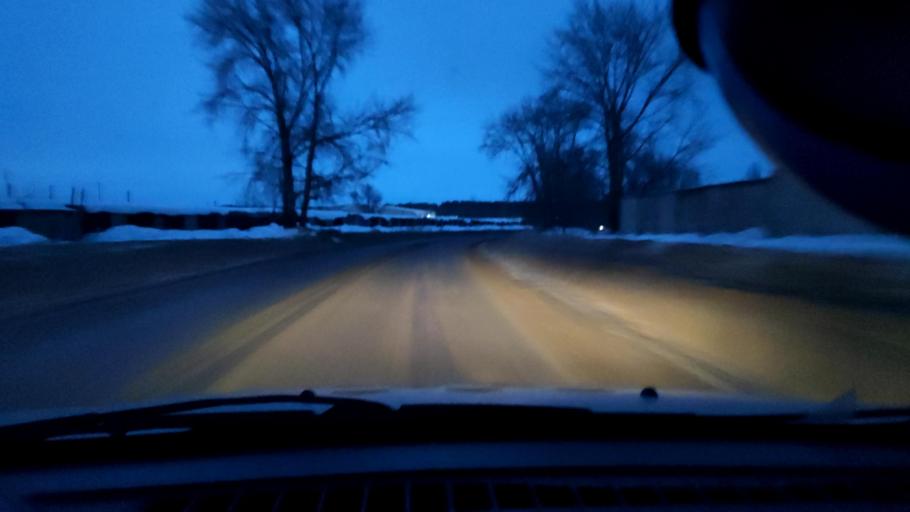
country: RU
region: Perm
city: Overyata
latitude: 58.0001
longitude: 55.9132
